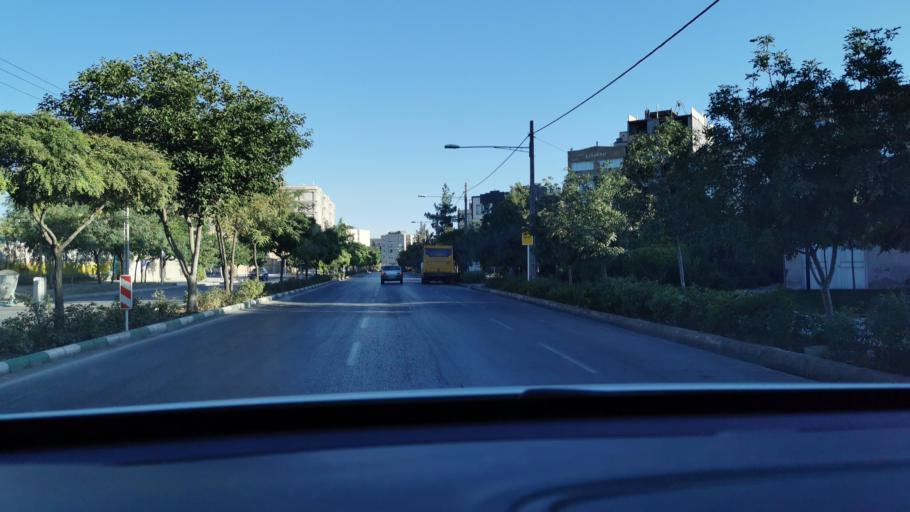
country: IR
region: Razavi Khorasan
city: Mashhad
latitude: 36.3584
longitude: 59.4855
